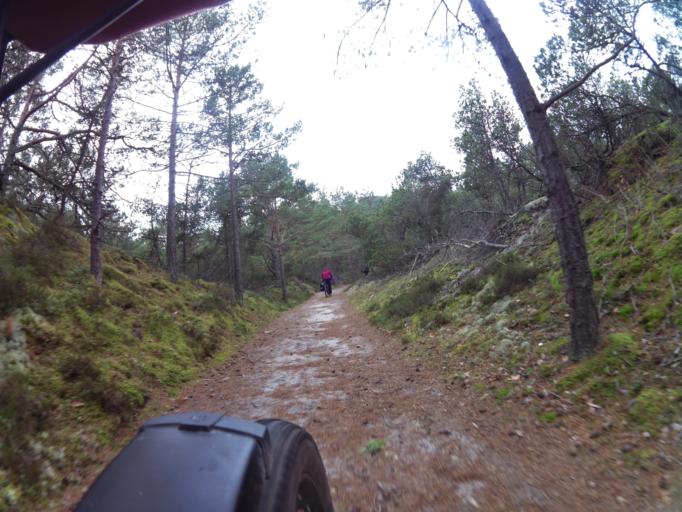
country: PL
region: Pomeranian Voivodeship
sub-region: Powiat pucki
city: Hel
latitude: 54.6283
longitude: 18.8062
